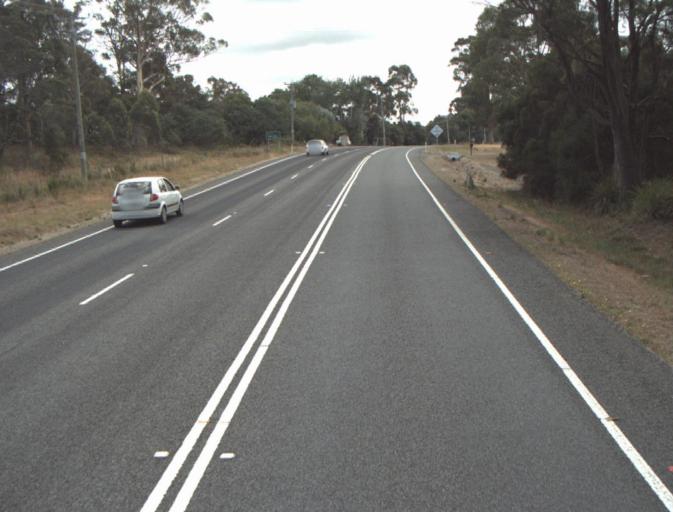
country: AU
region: Tasmania
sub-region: Launceston
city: Mayfield
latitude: -41.2872
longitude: 147.0413
